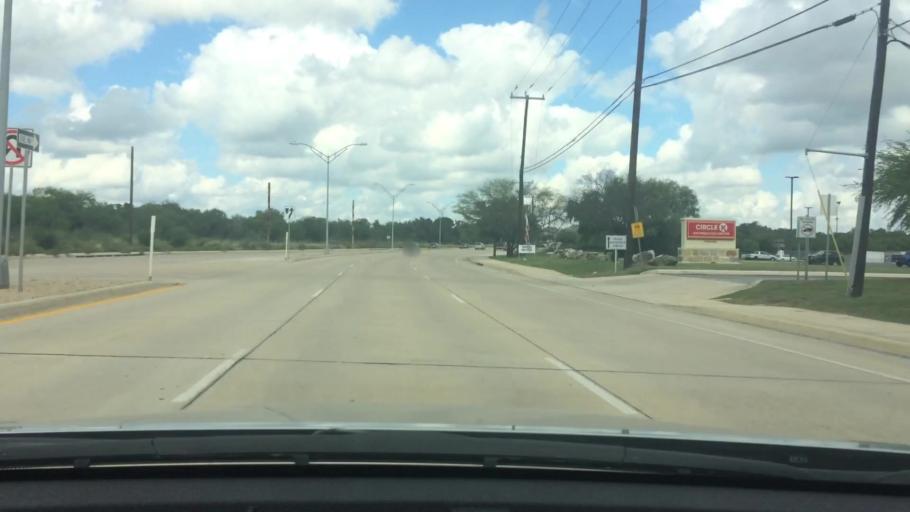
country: US
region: Texas
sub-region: Bexar County
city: Hollywood Park
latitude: 29.6251
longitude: -98.4237
